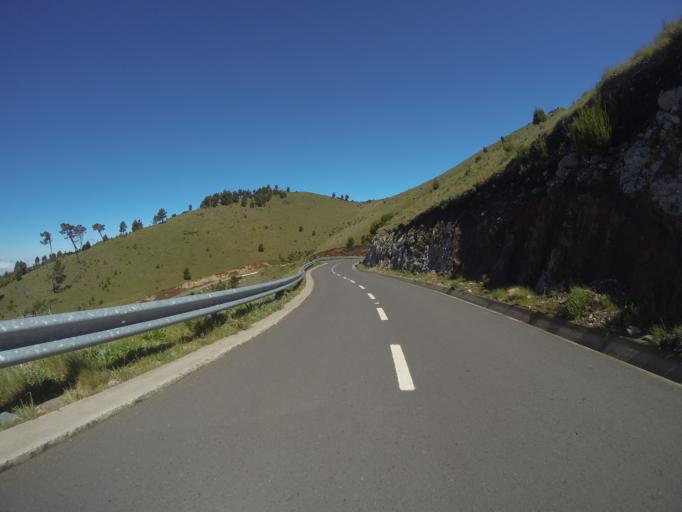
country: PT
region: Madeira
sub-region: Camara de Lobos
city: Curral das Freiras
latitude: 32.7120
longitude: -16.9551
